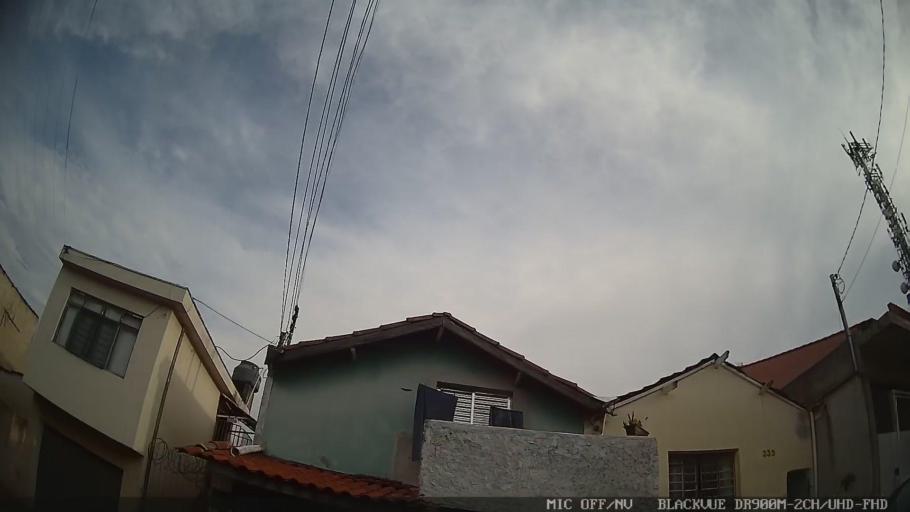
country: BR
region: Sao Paulo
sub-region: Braganca Paulista
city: Braganca Paulista
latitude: -22.9492
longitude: -46.5480
